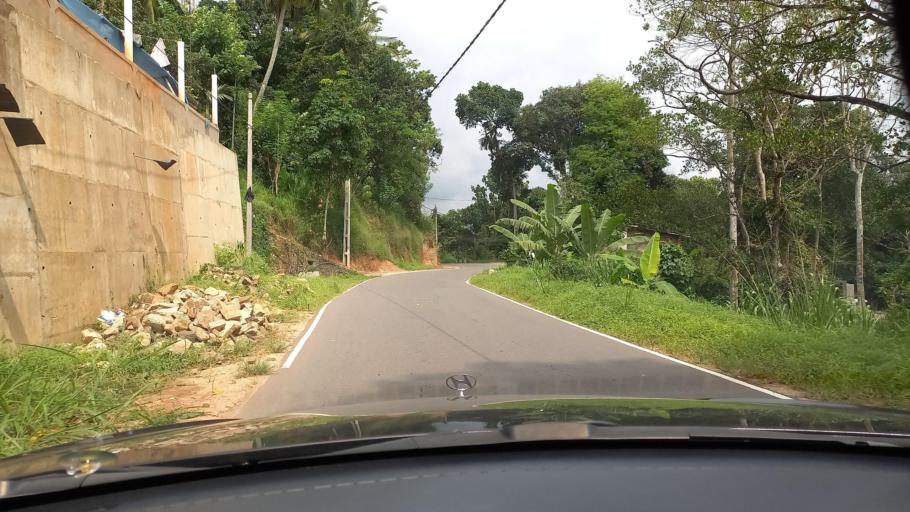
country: LK
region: Central
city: Gampola
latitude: 7.2125
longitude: 80.6153
